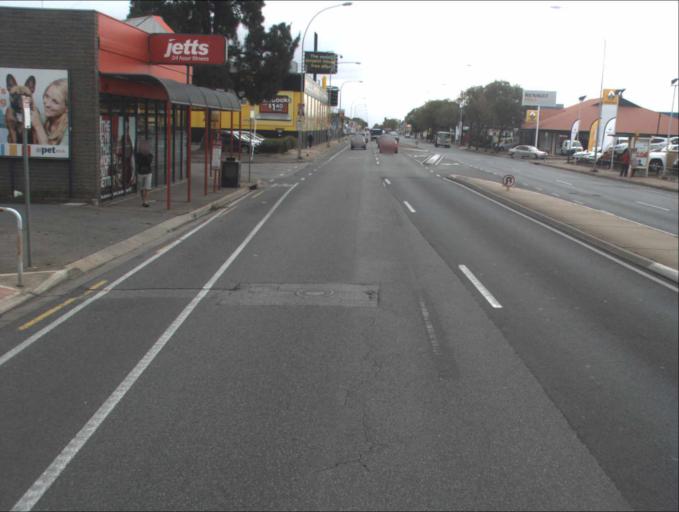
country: AU
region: South Australia
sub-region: Prospect
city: Prospect
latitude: -34.8910
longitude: 138.6033
